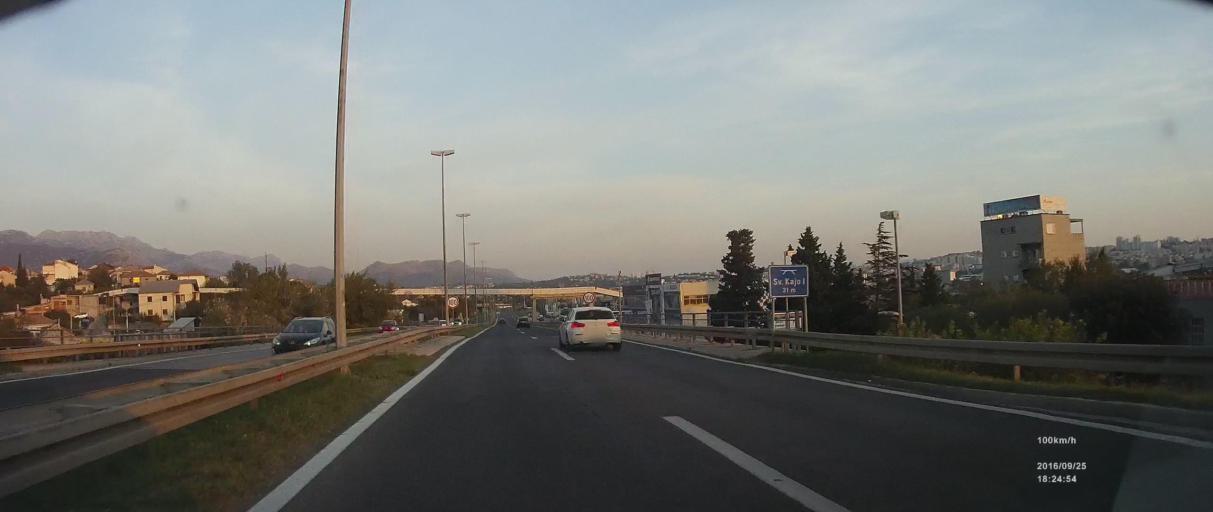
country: HR
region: Splitsko-Dalmatinska
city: Vranjic
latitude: 43.5420
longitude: 16.4652
